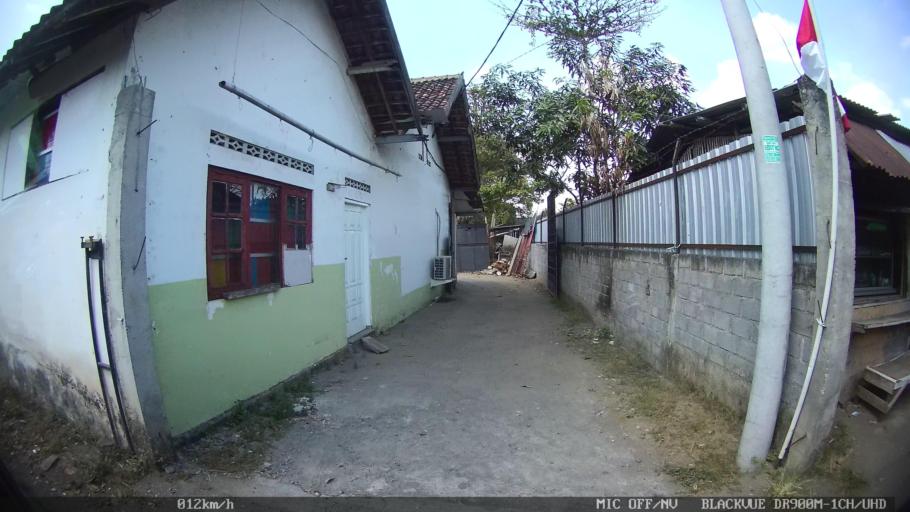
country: ID
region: Daerah Istimewa Yogyakarta
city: Kasihan
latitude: -7.8325
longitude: 110.3759
